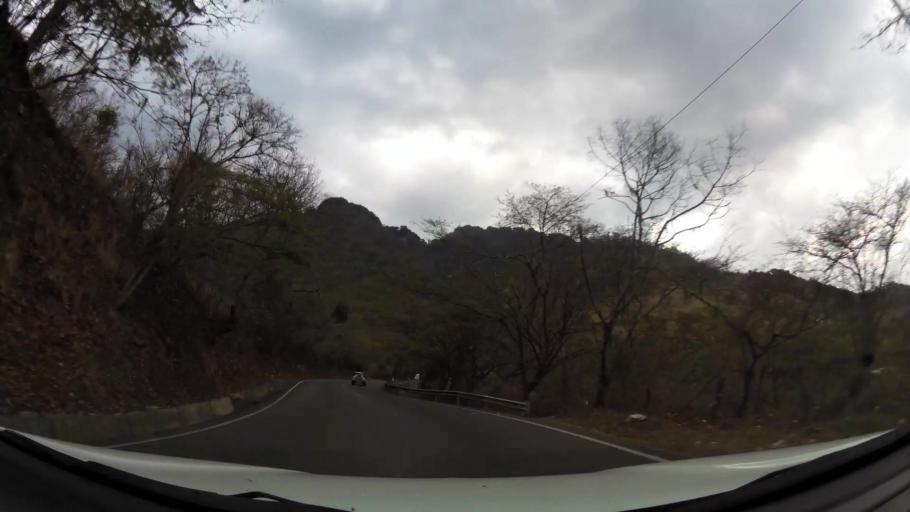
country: NI
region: Jinotega
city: Jinotega
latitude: 13.0734
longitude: -85.9879
